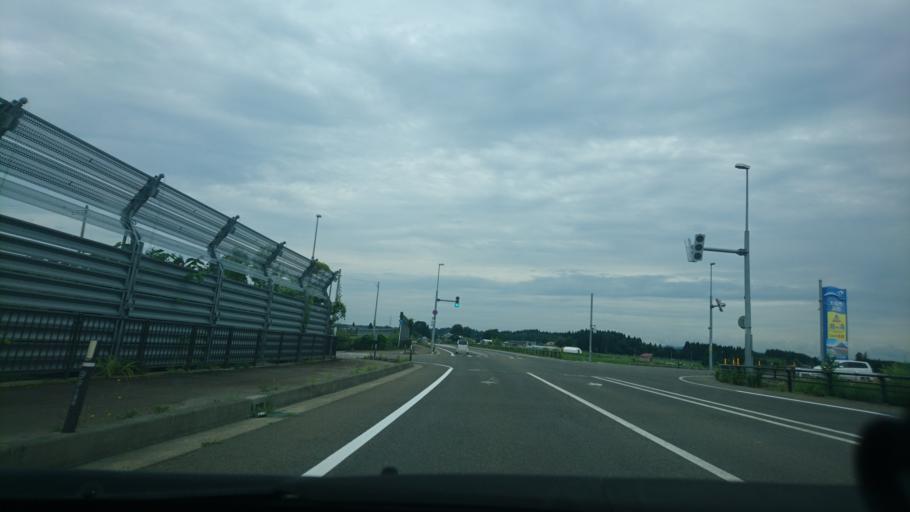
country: JP
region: Akita
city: Omagari
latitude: 39.4952
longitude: 140.4486
